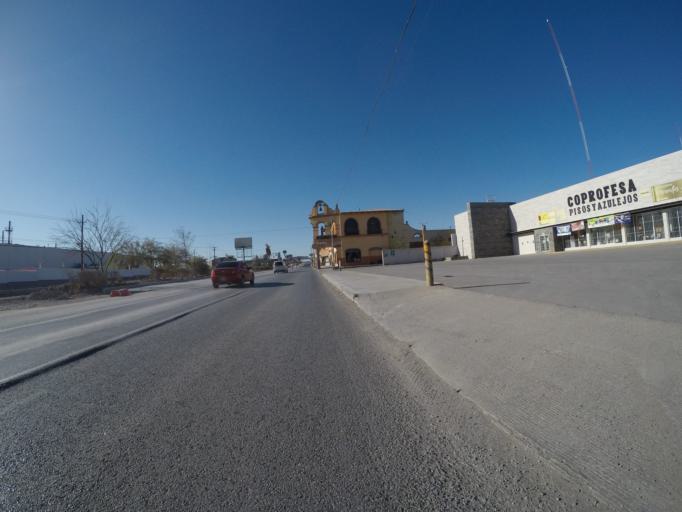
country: MX
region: Chihuahua
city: Ciudad Juarez
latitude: 31.6814
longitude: -106.4248
